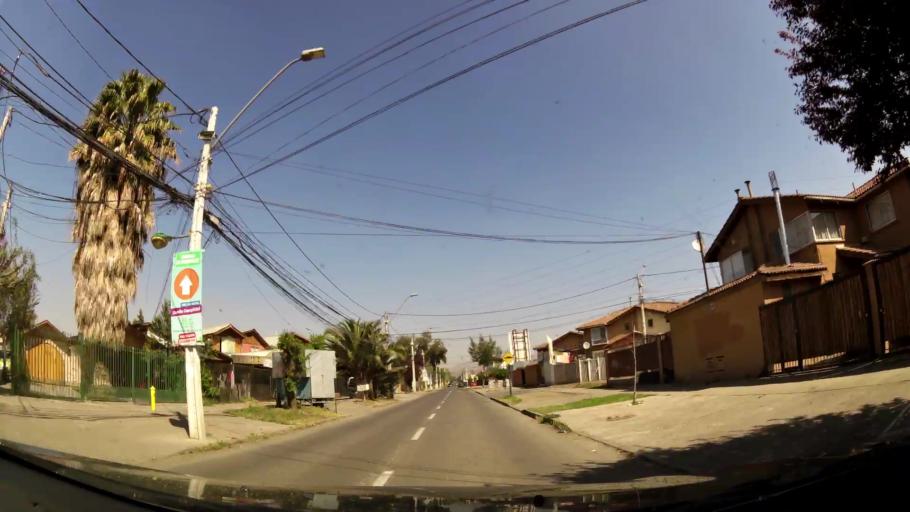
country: CL
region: Santiago Metropolitan
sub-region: Provincia de Santiago
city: Lo Prado
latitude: -33.3532
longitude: -70.7340
